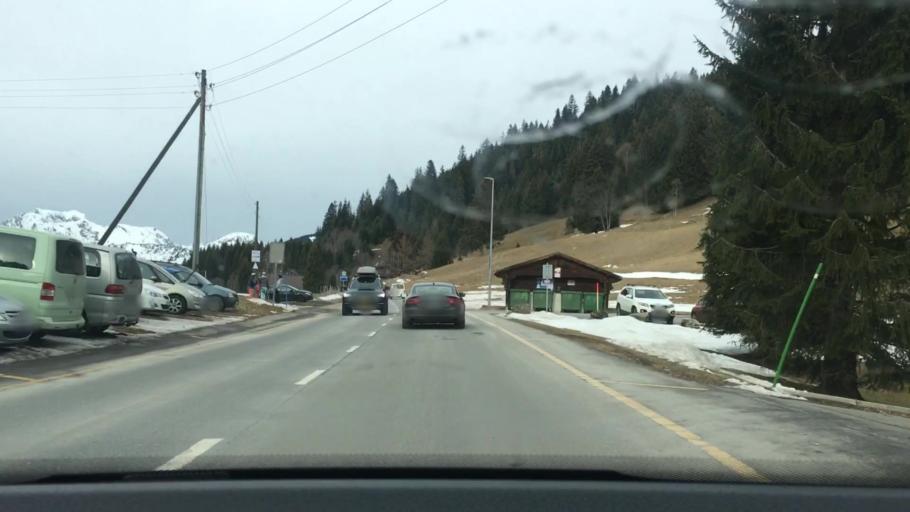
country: FR
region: Rhone-Alpes
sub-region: Departement de la Haute-Savoie
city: Chatel
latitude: 46.2434
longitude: 6.8508
